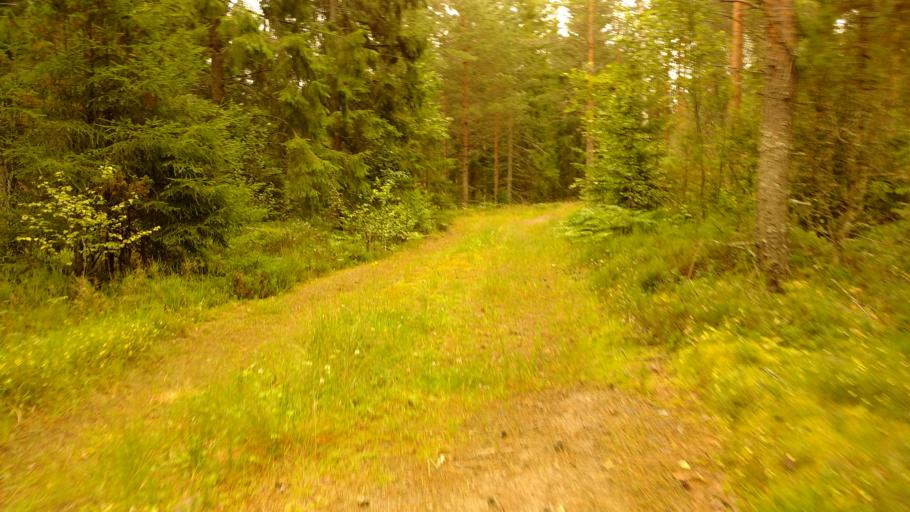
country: FI
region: Varsinais-Suomi
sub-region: Salo
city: Pertteli
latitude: 60.4092
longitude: 23.2283
